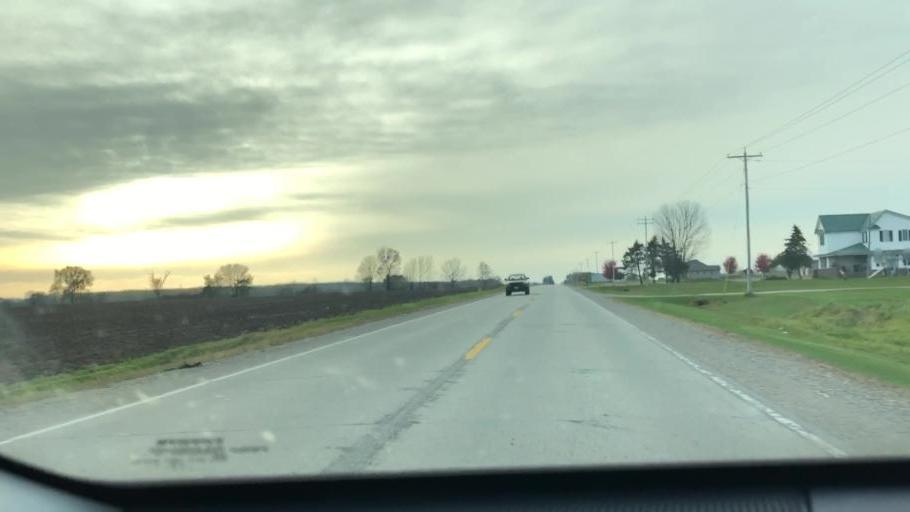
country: US
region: Wisconsin
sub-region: Outagamie County
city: Seymour
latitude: 44.4438
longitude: -88.3022
